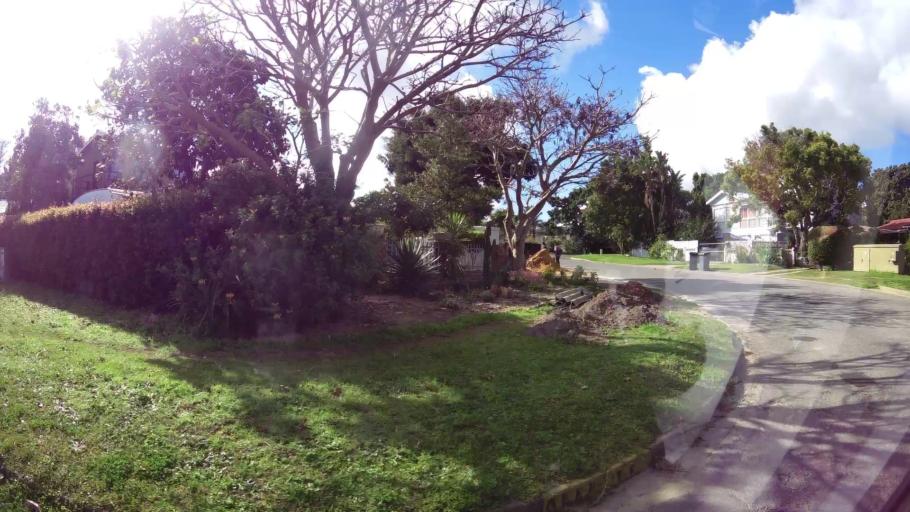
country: ZA
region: Western Cape
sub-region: Eden District Municipality
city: Knysna
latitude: -34.0429
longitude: 23.0741
